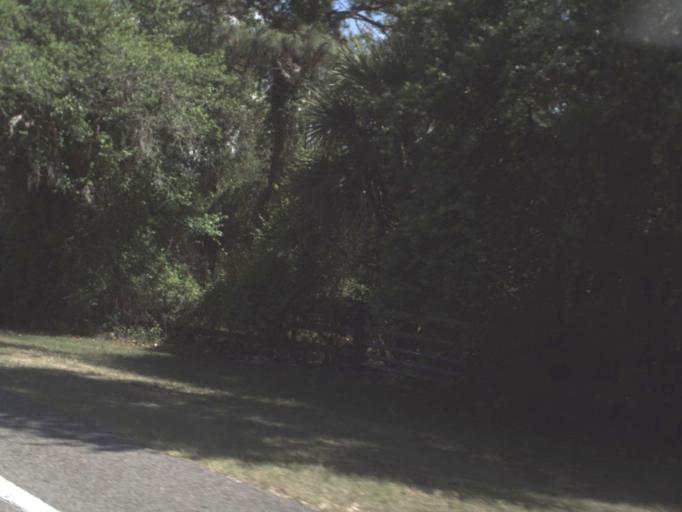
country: US
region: Florida
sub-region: Lake County
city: Mount Plymouth
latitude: 28.8117
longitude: -81.4652
